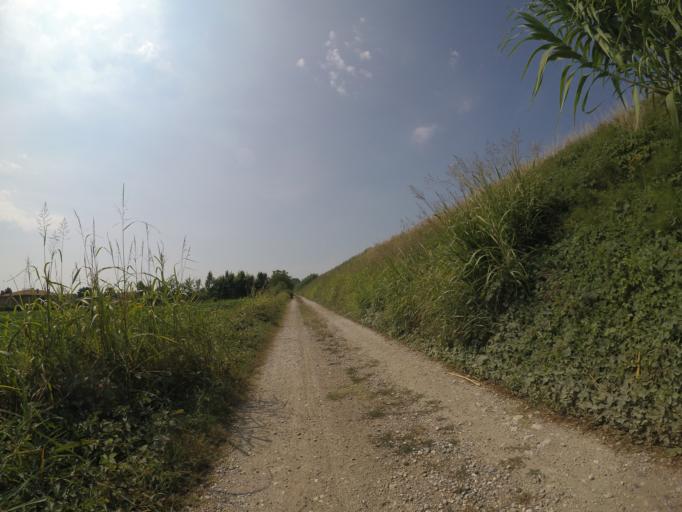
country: IT
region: Friuli Venezia Giulia
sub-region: Provincia di Udine
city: Pertegada
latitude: 45.7171
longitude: 13.0412
